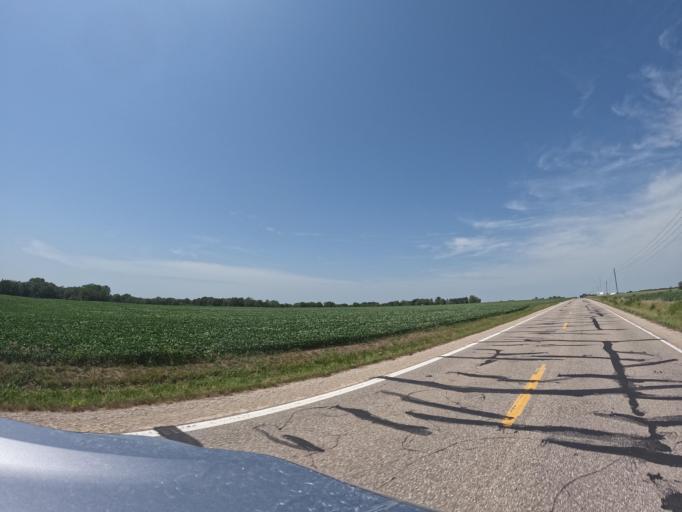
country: US
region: Iowa
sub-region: Henry County
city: Mount Pleasant
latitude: 40.9911
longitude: -91.6123
